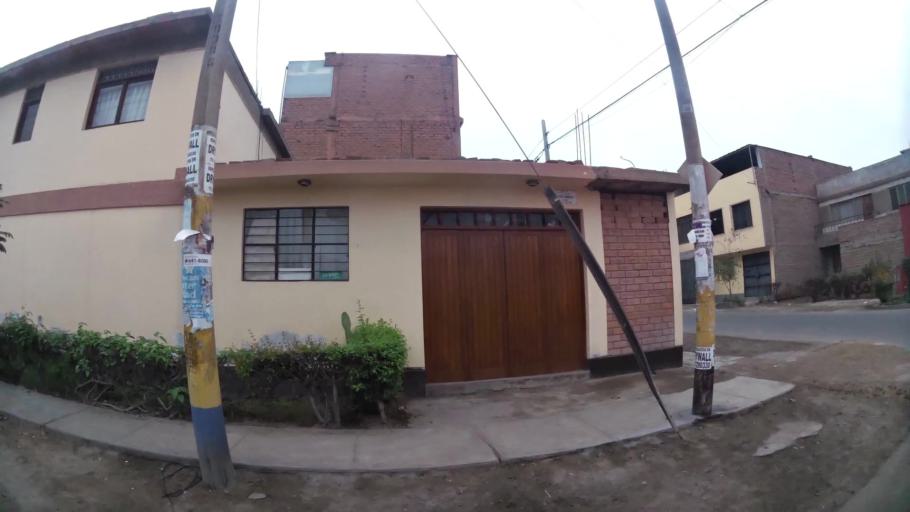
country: PE
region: Lima
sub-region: Lima
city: Surco
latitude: -12.1664
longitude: -76.9707
